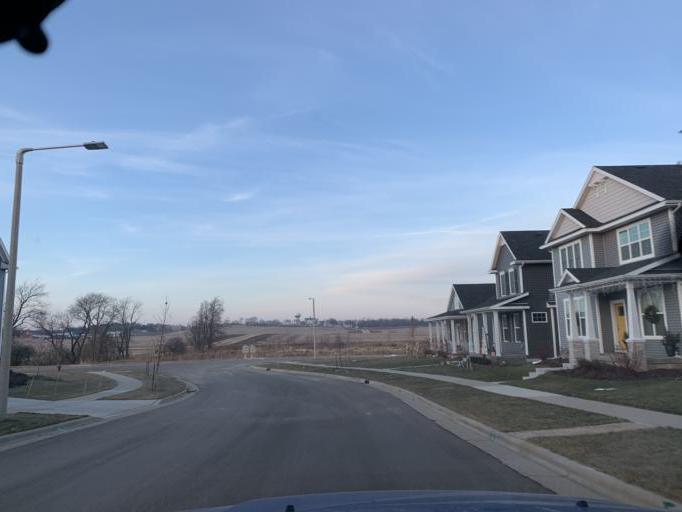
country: US
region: Wisconsin
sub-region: Dane County
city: Middleton
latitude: 43.0583
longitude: -89.5662
